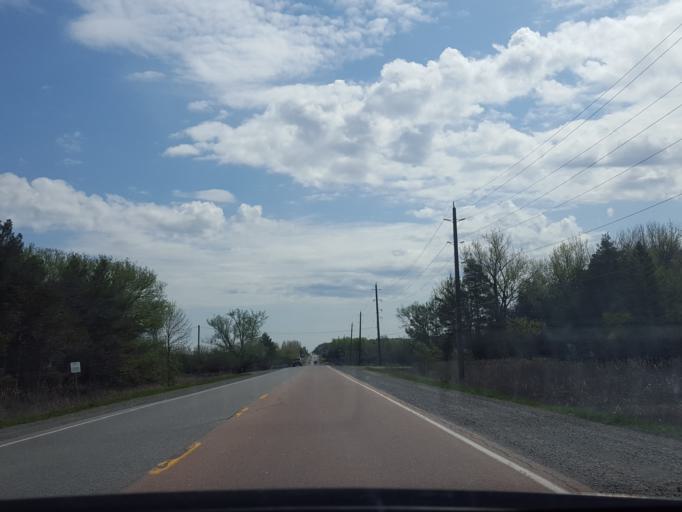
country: CA
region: Ontario
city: Oshawa
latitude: 44.1057
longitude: -78.8820
